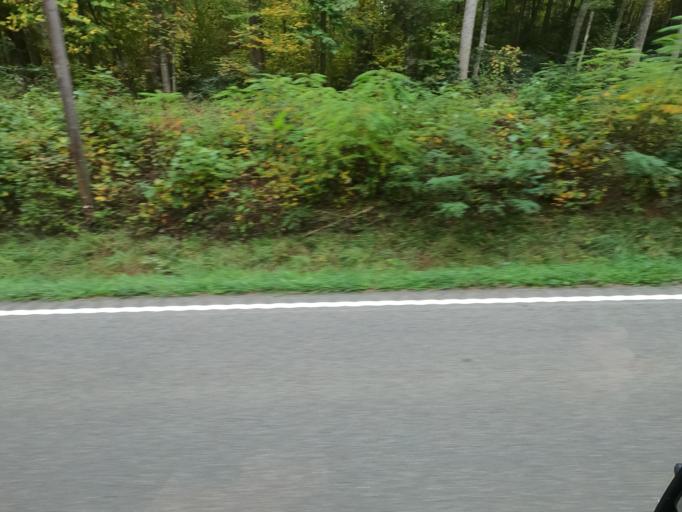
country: US
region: Tennessee
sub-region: Carter County
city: Elizabethton
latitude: 36.2604
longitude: -82.2147
